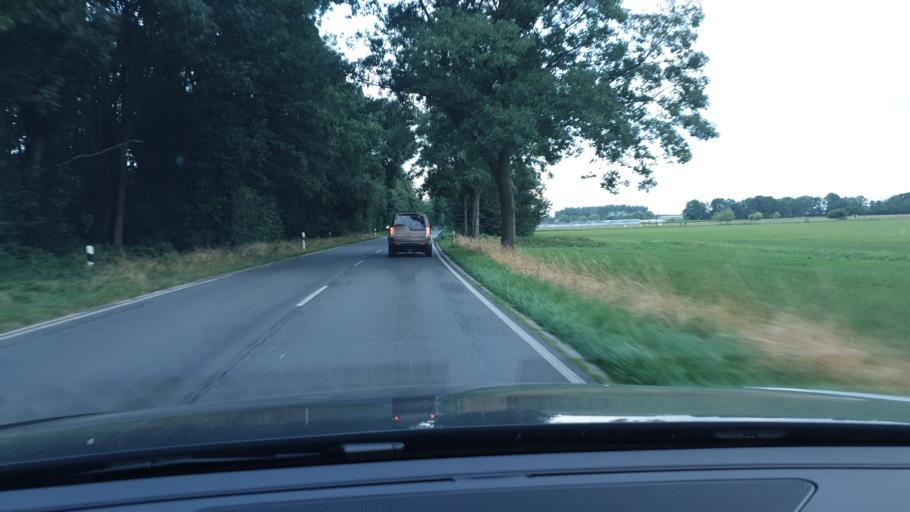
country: DE
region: North Rhine-Westphalia
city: Straelen
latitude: 51.4501
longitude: 6.2405
